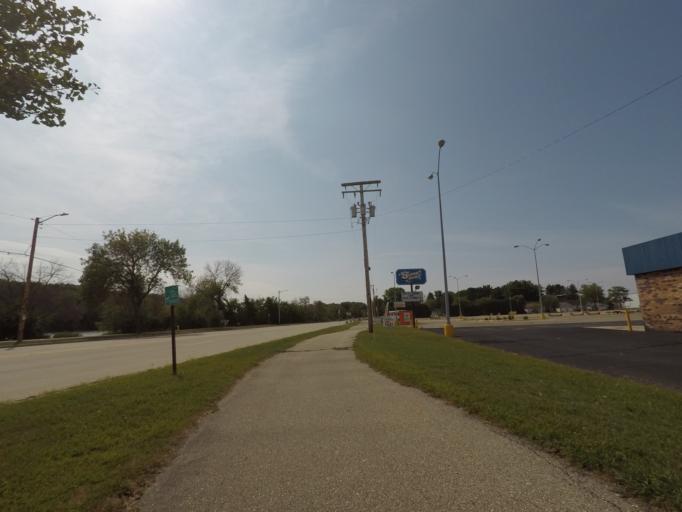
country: US
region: Wisconsin
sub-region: Jefferson County
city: Fort Atkinson
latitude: 42.9438
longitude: -88.8279
